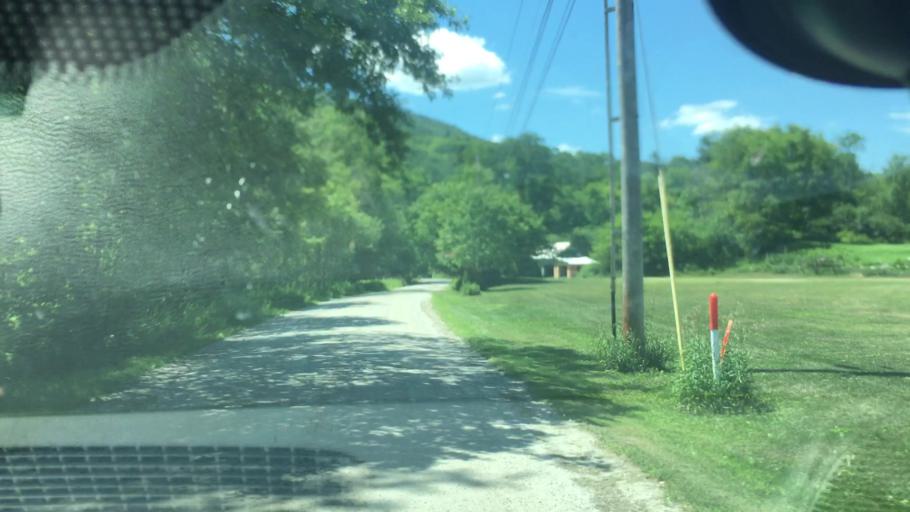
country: US
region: Vermont
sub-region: Windsor County
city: Chester
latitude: 43.4306
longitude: -72.7146
